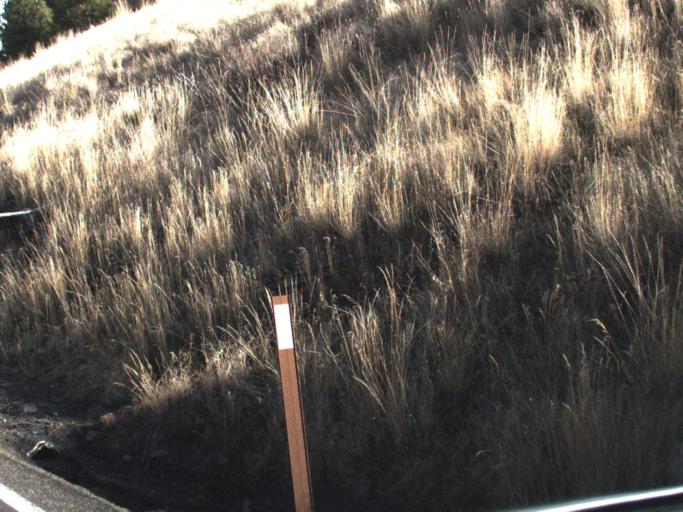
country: US
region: Washington
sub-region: Whitman County
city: Colfax
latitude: 46.8811
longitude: -117.3598
